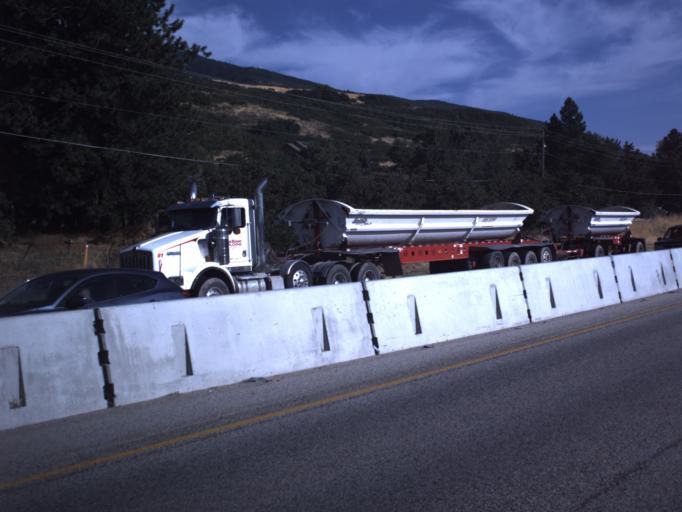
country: US
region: Utah
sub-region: Davis County
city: Fruit Heights
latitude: 41.0717
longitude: -111.9110
